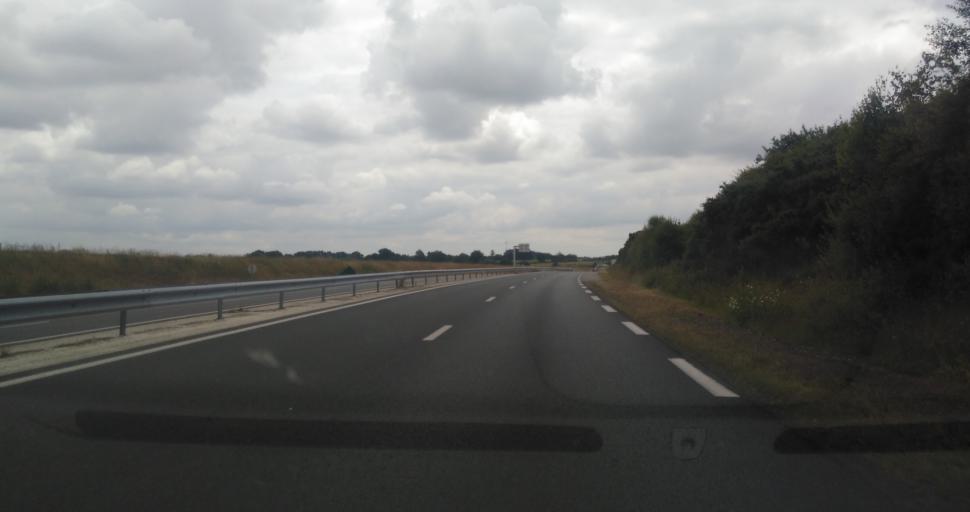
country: FR
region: Pays de la Loire
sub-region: Departement de la Vendee
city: La Chaize-le-Vicomte
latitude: 46.6592
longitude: -1.2458
